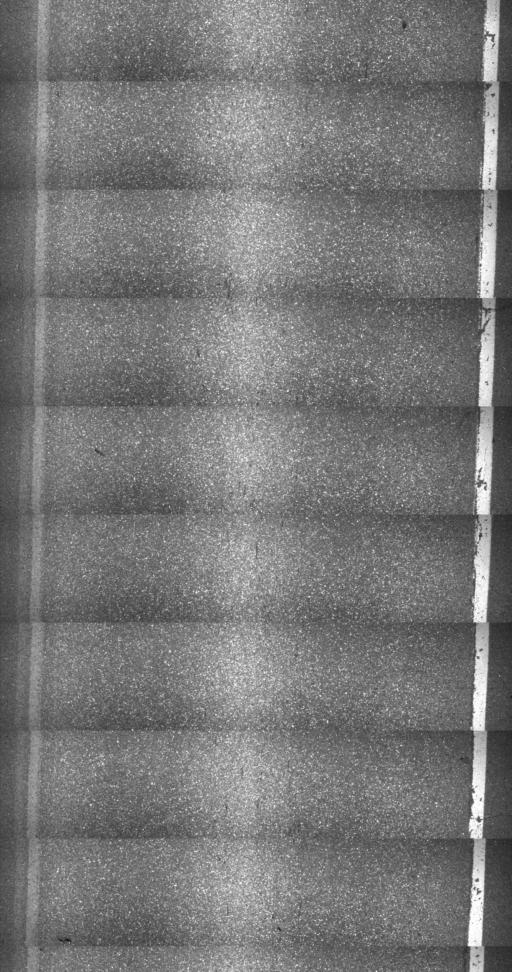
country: US
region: Vermont
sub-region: Lamoille County
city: Johnson
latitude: 44.6464
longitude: -72.8661
